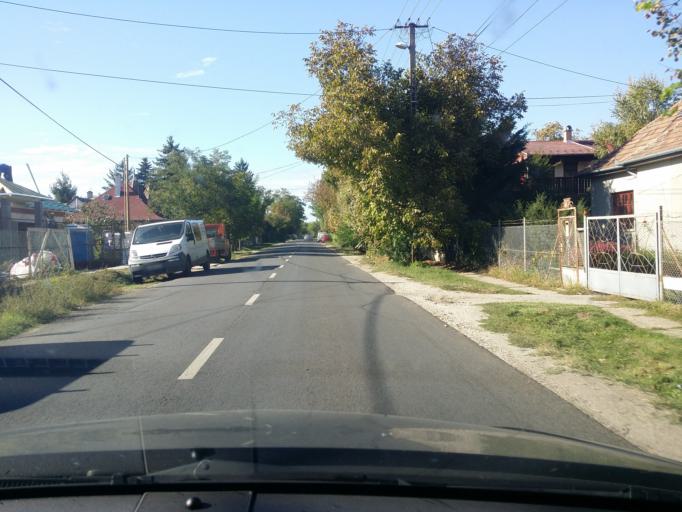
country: HU
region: Pest
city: God
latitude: 47.7011
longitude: 19.1498
